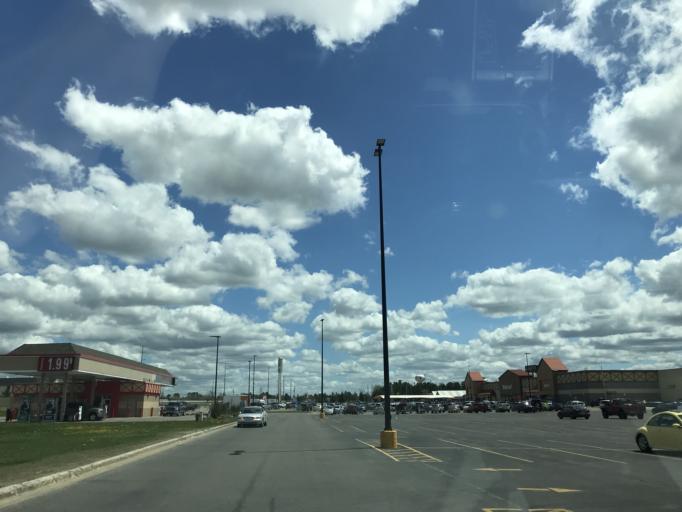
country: US
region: Michigan
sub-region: Otsego County
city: Gaylord
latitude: 45.0237
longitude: -84.6926
